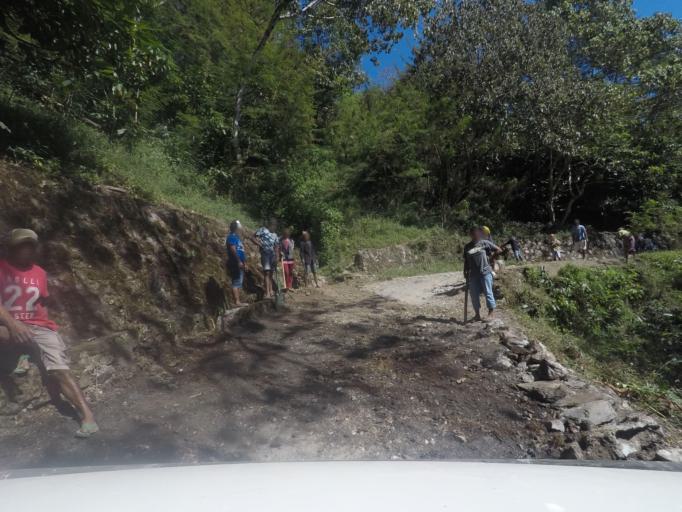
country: TL
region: Ermera
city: Gleno
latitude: -8.7264
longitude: 125.3324
